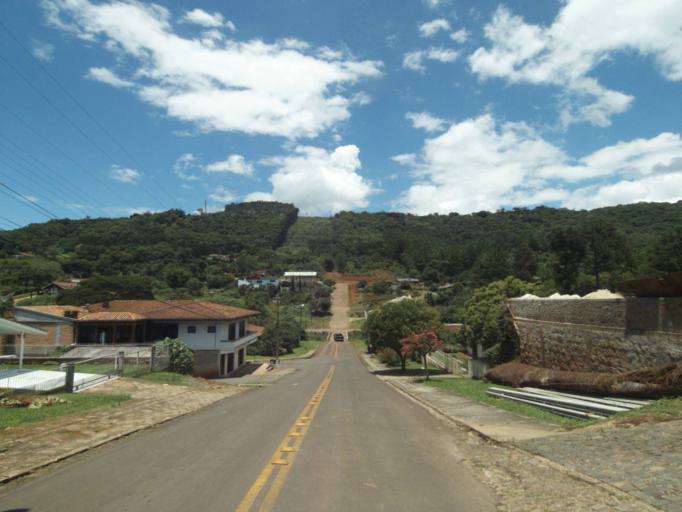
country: BR
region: Parana
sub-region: Uniao Da Vitoria
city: Uniao da Vitoria
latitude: -26.1609
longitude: -51.5543
